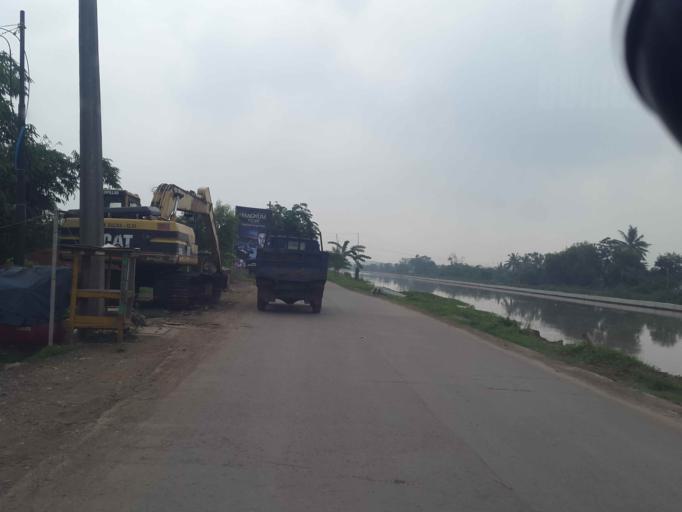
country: ID
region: West Java
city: Cikarang
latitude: -6.3463
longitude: 107.2151
